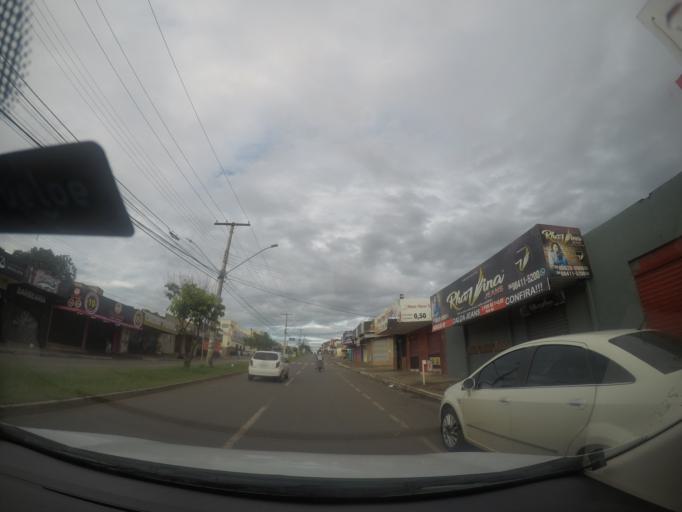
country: BR
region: Goias
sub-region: Goiania
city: Goiania
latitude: -16.6146
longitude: -49.3454
